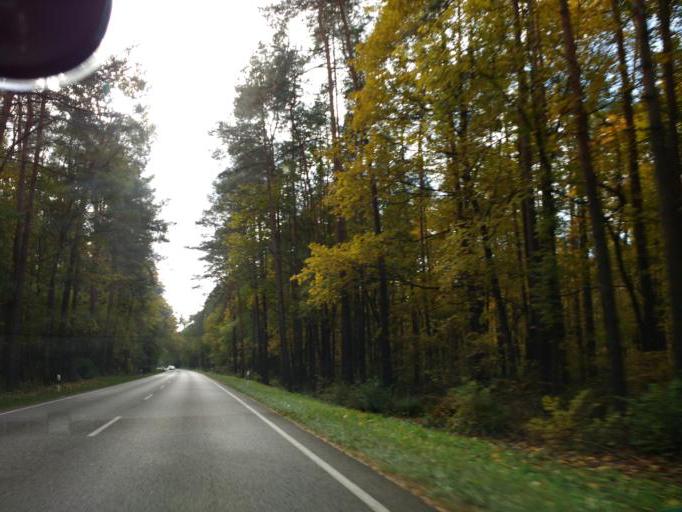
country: DE
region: Brandenburg
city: Petershagen
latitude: 52.5109
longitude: 13.8023
